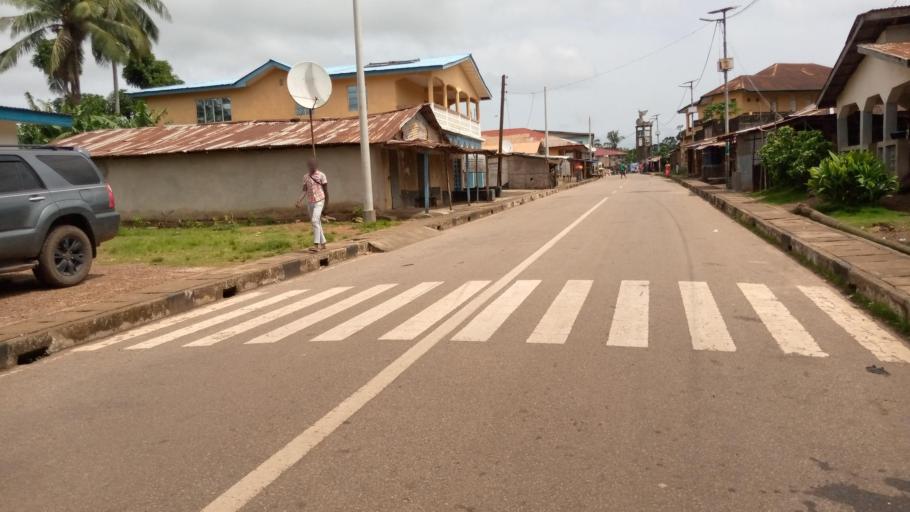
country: SL
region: Southern Province
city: Moyamba
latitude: 8.1589
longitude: -12.4320
